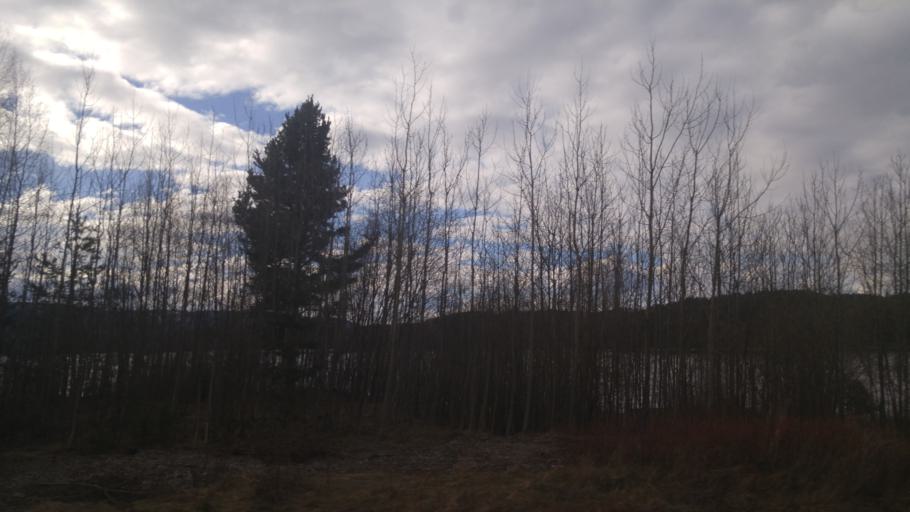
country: NO
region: Hedmark
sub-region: Stange
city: Stange
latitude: 60.5817
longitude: 11.2711
